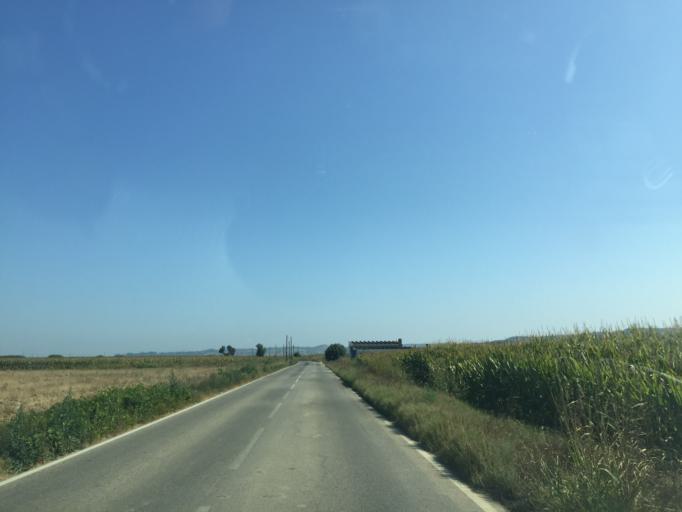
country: PT
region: Santarem
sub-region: Alpiarca
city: Alpiarca
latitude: 39.2993
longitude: -8.5197
